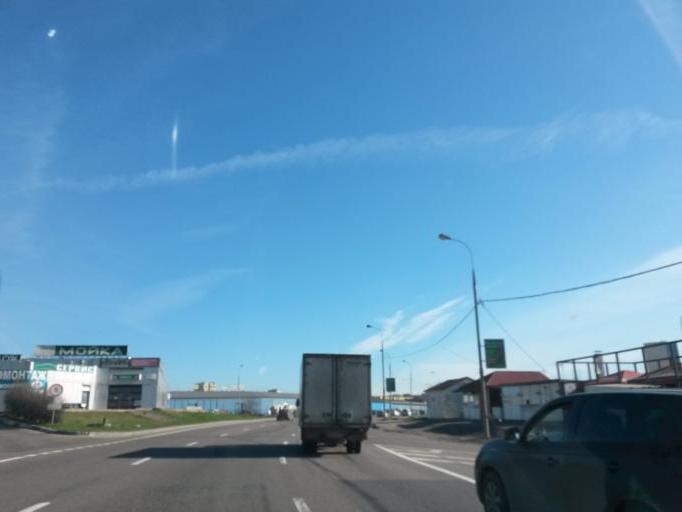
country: RU
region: Moscow
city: Annino
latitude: 55.5713
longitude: 37.6004
